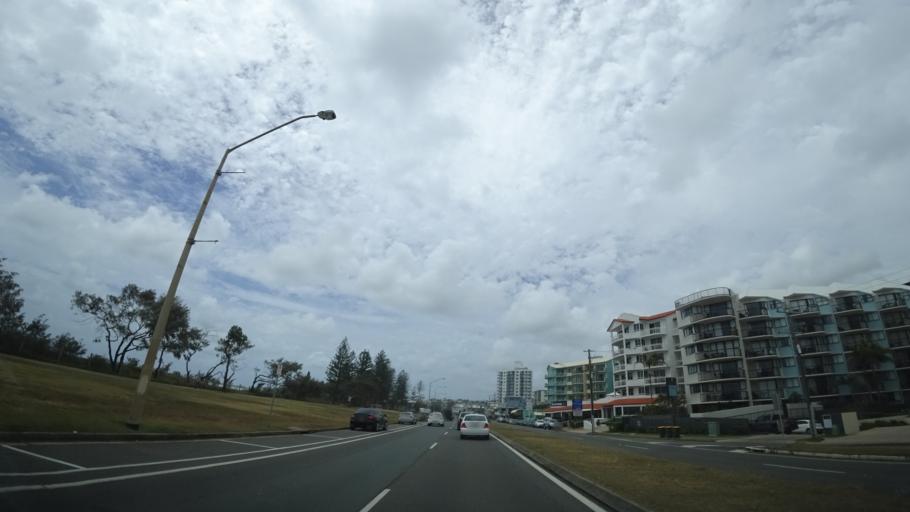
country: AU
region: Queensland
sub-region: Sunshine Coast
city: Mooloolaba
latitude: -26.6660
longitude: 153.1061
